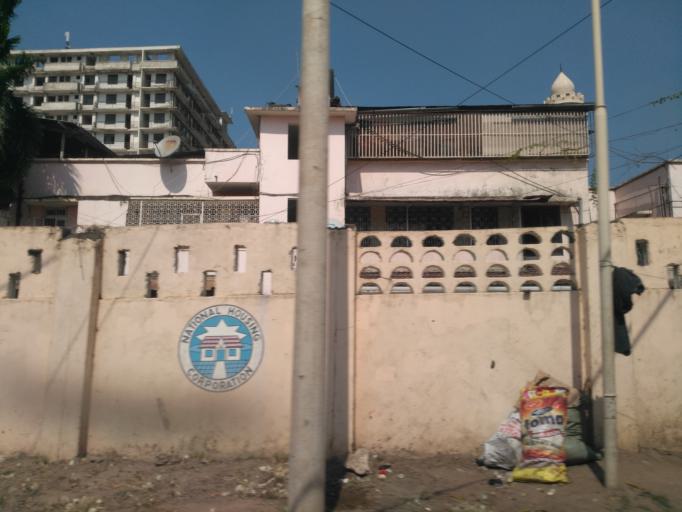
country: TZ
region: Dar es Salaam
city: Dar es Salaam
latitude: -6.8041
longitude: 39.2836
